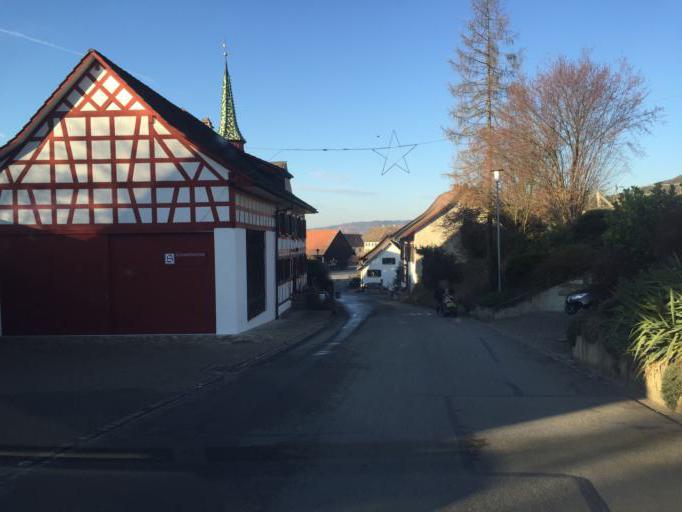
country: CH
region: Thurgau
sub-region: Frauenfeld District
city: Diessenhofen
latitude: 47.6620
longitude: 8.7687
